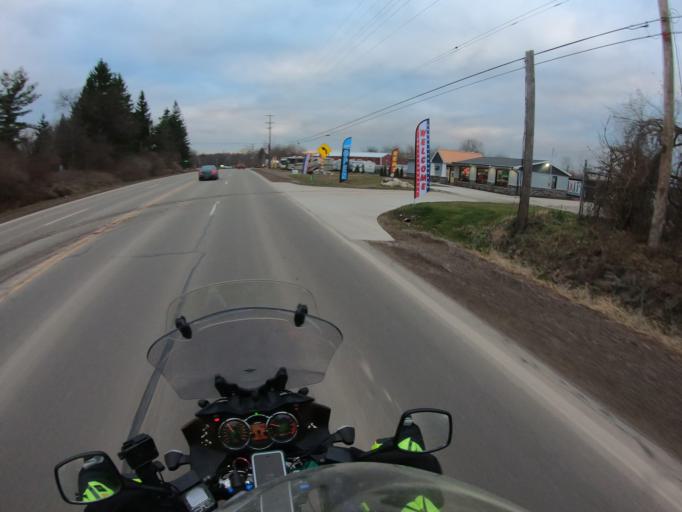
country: US
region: Michigan
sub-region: Oakland County
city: Holly
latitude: 42.8481
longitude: -83.5670
